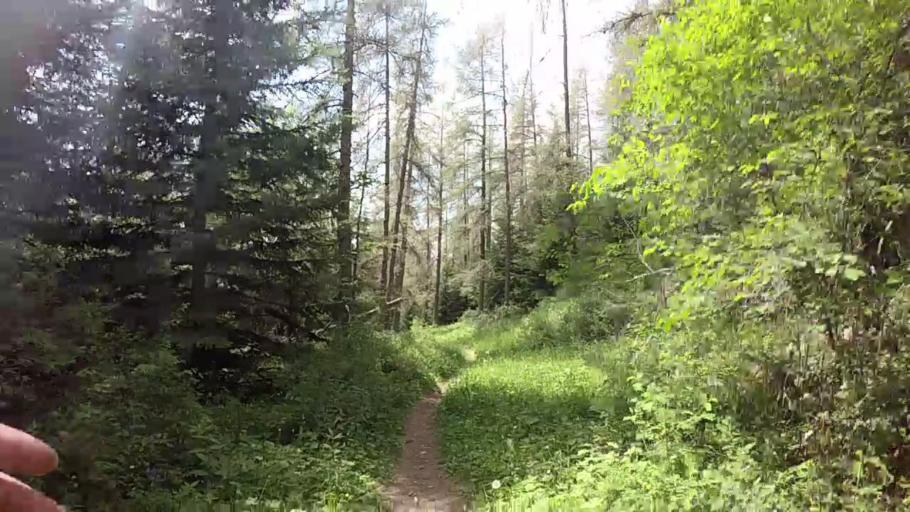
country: FR
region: Provence-Alpes-Cote d'Azur
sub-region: Departement des Alpes-de-Haute-Provence
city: Seyne-les-Alpes
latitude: 44.4091
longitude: 6.3675
